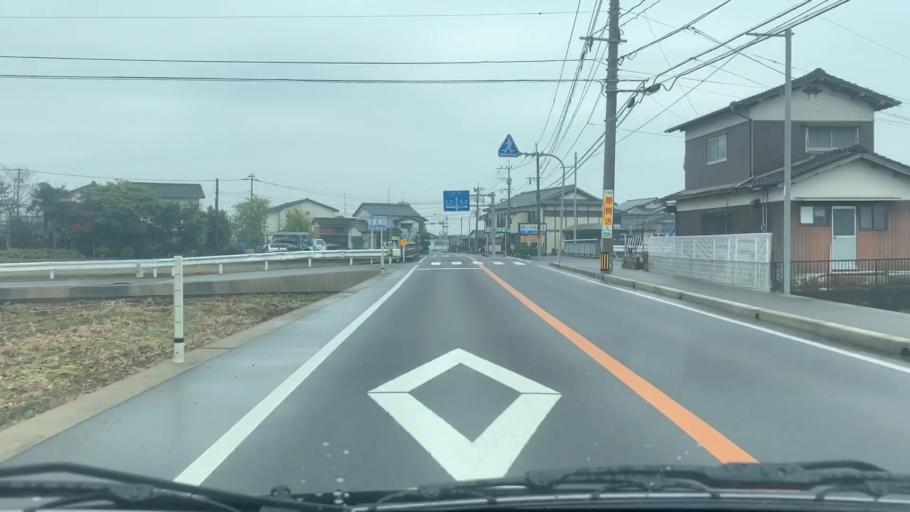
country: JP
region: Saga Prefecture
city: Takeocho-takeo
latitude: 33.1955
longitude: 130.1127
